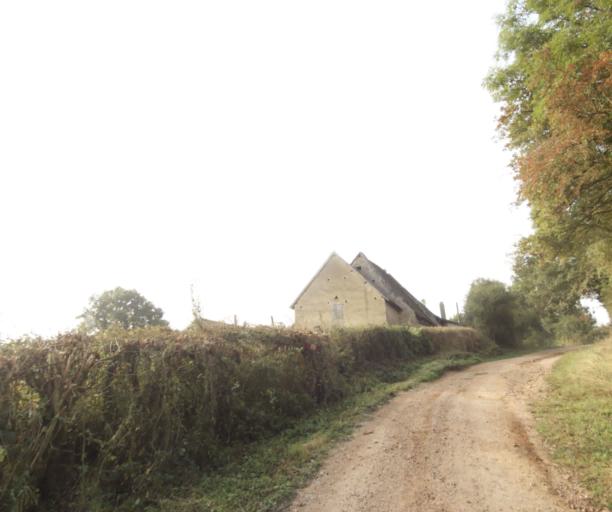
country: FR
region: Bourgogne
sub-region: Departement de Saone-et-Loire
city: Charolles
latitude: 46.4438
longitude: 4.2869
